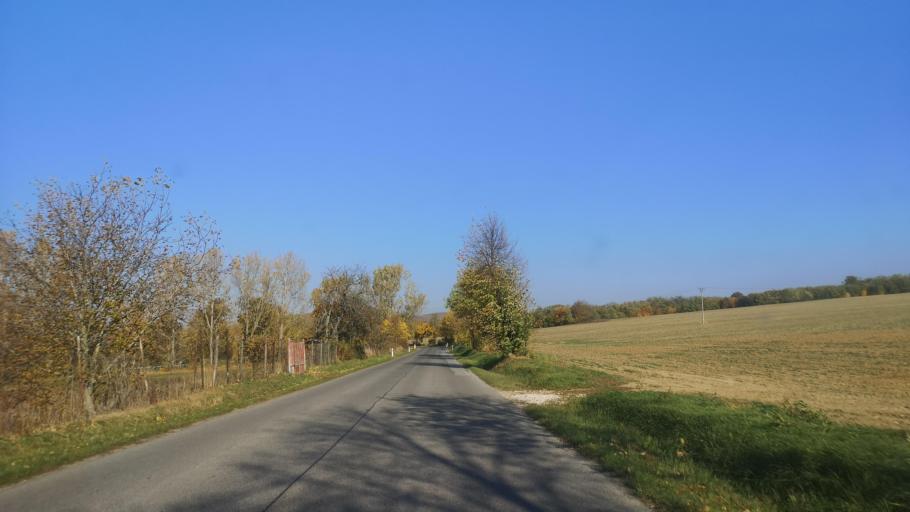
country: SK
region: Nitriansky
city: Zlate Moravce
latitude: 48.4219
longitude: 18.4214
